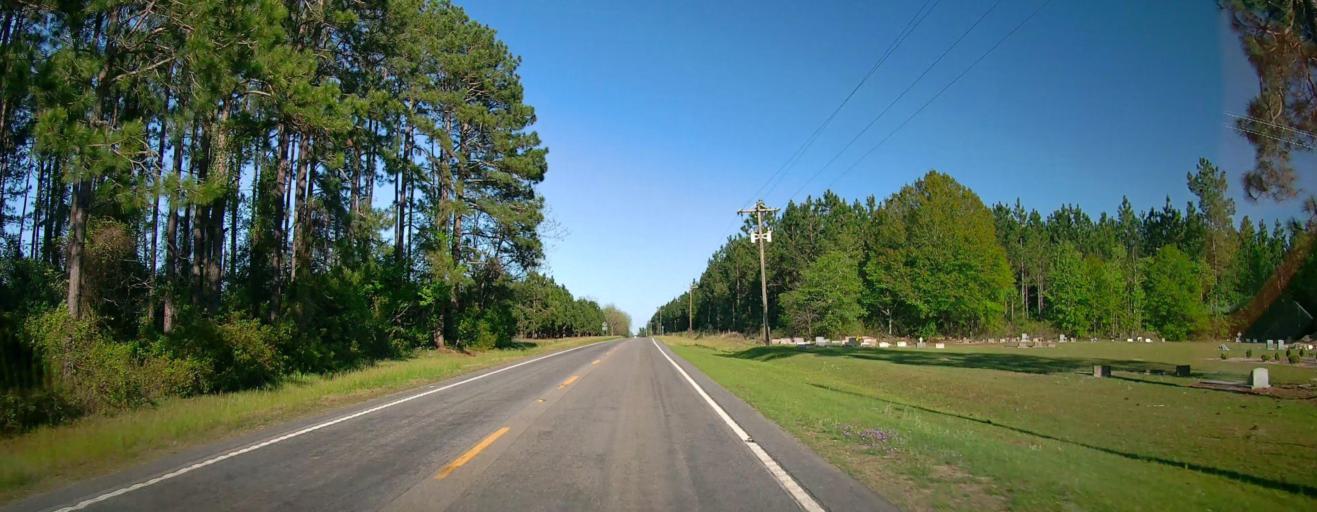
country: US
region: Georgia
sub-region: Ben Hill County
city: Fitzgerald
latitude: 31.7186
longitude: -83.3400
